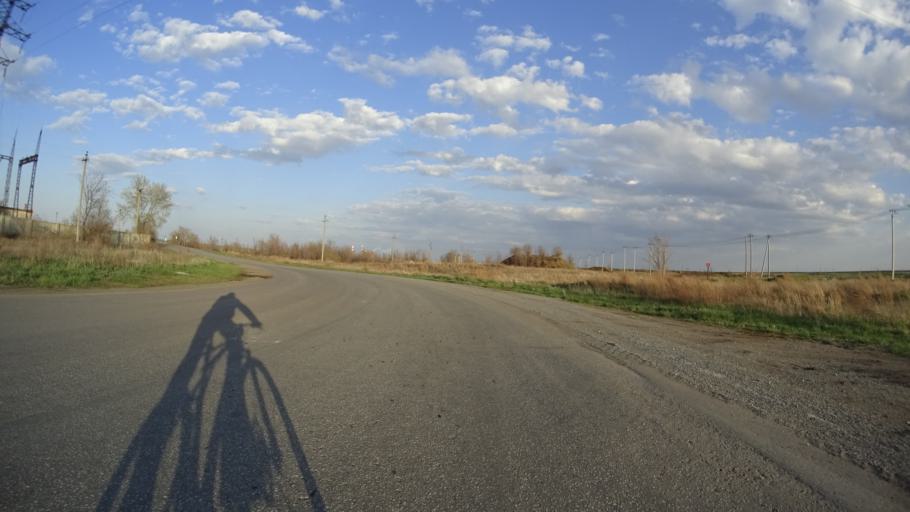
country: RU
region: Chelyabinsk
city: Troitsk
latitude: 54.0624
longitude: 61.5719
